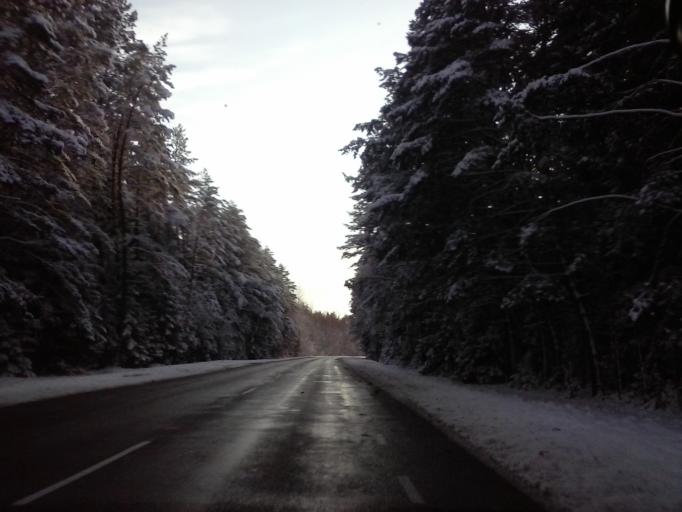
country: EE
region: Tartu
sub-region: UElenurme vald
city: Ulenurme
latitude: 58.3346
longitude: 26.8943
